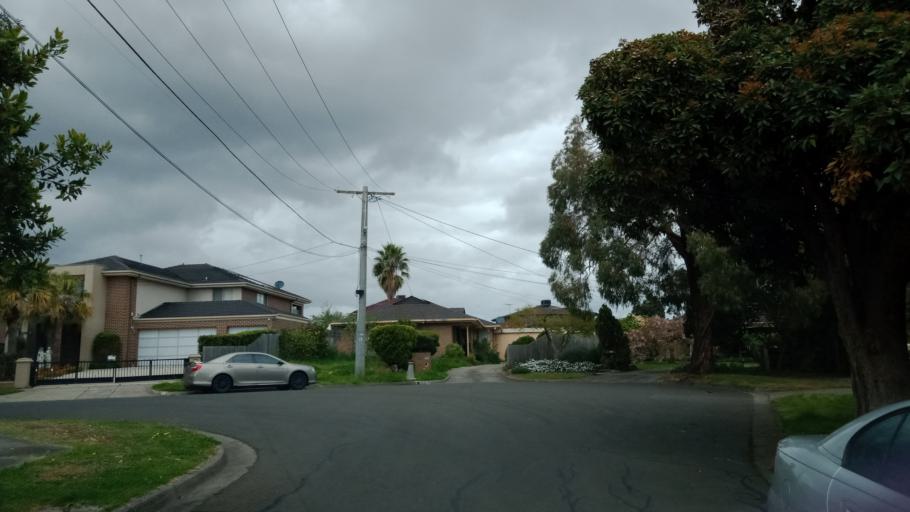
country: AU
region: Victoria
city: Burwood East
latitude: -37.8703
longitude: 145.1515
